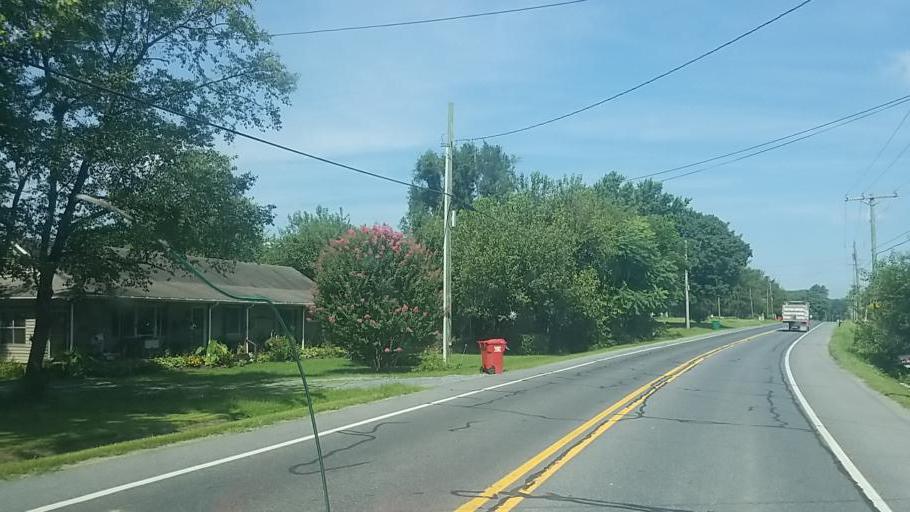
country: US
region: Delaware
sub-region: Sussex County
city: Seaford
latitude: 38.6689
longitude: -75.5715
